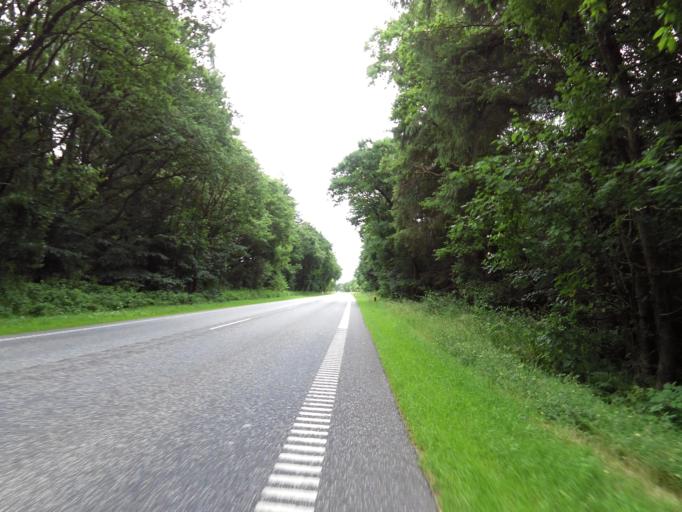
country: DK
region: South Denmark
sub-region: Tonder Kommune
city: Logumkloster
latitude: 55.0972
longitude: 8.9396
